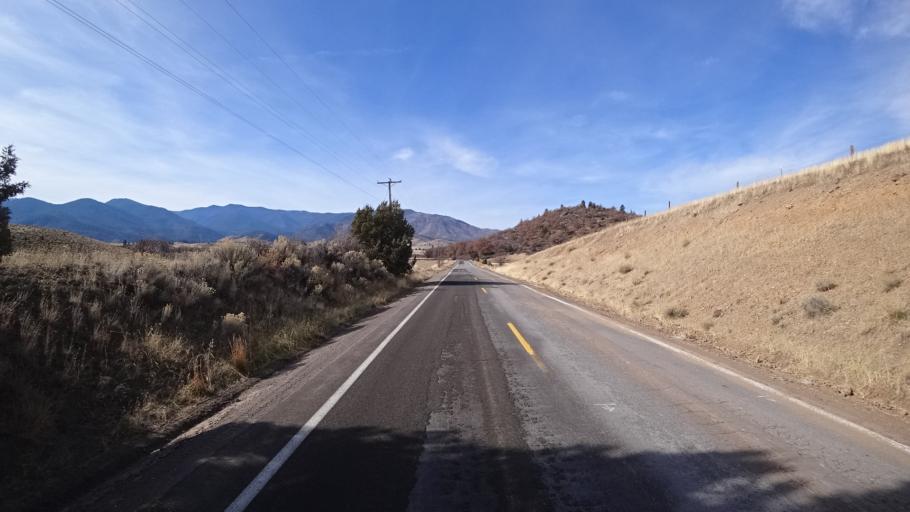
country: US
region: California
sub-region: Siskiyou County
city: Weed
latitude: 41.4678
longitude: -122.4216
